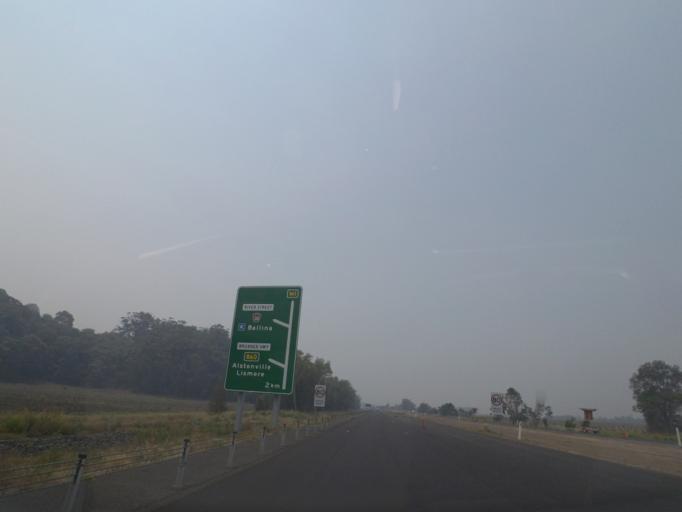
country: AU
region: New South Wales
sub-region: Ballina
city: Ballina
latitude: -28.8819
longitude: 153.4852
